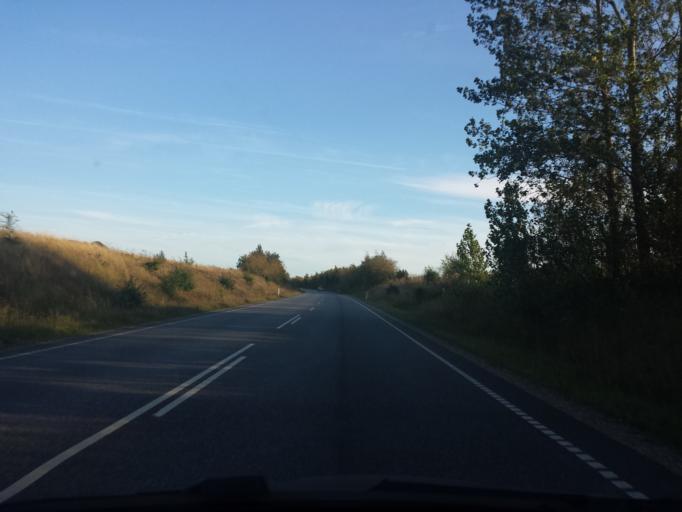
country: DK
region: Zealand
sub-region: Roskilde Kommune
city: Jyllinge
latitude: 55.8013
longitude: 12.1031
